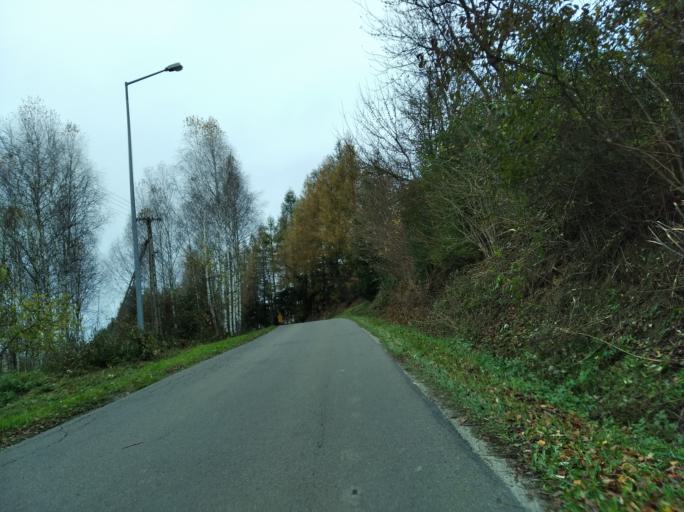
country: PL
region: Subcarpathian Voivodeship
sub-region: Powiat krosnienski
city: Leki
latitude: 49.8279
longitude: 21.6370
